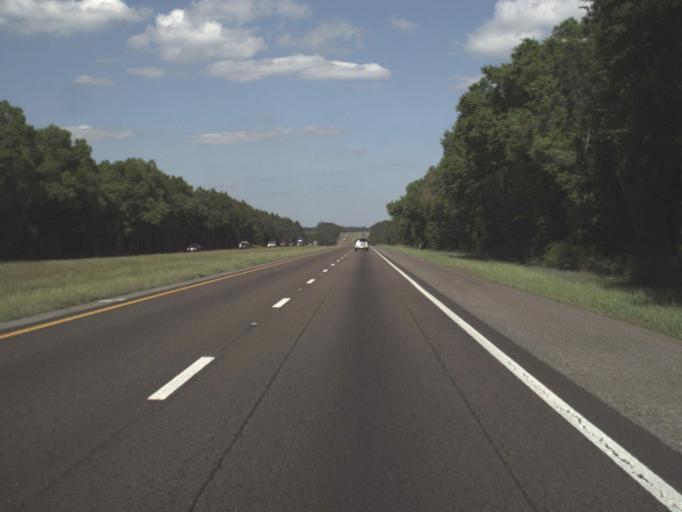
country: US
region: Florida
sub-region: Santa Rosa County
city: East Milton
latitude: 30.6584
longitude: -86.8728
